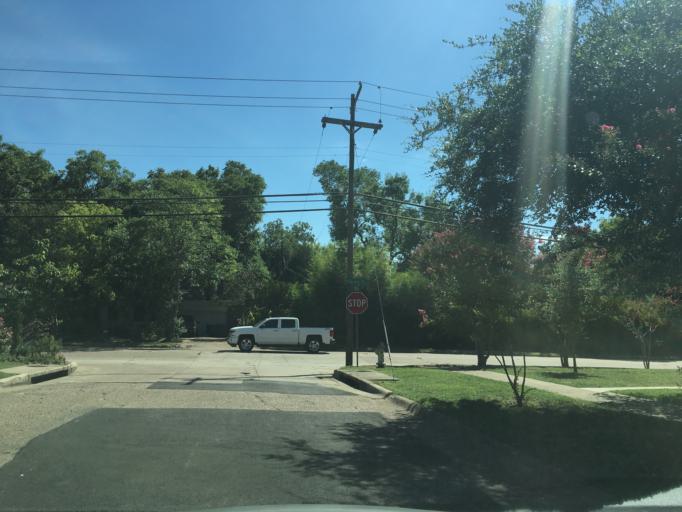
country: US
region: Texas
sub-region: Dallas County
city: Garland
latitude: 32.8409
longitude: -96.6984
